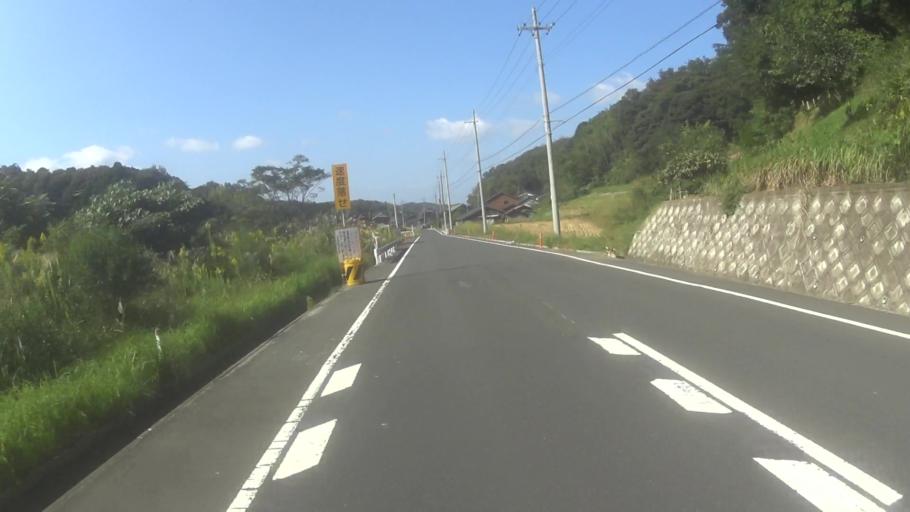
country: JP
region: Kyoto
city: Miyazu
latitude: 35.6746
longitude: 135.0553
